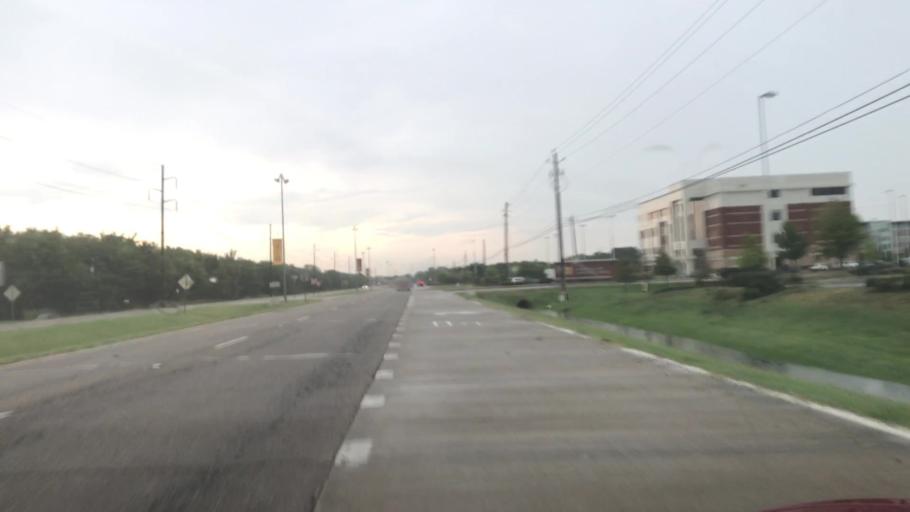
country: US
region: Louisiana
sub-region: Bossier Parish
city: Red Chute
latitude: 32.5416
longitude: -93.6468
